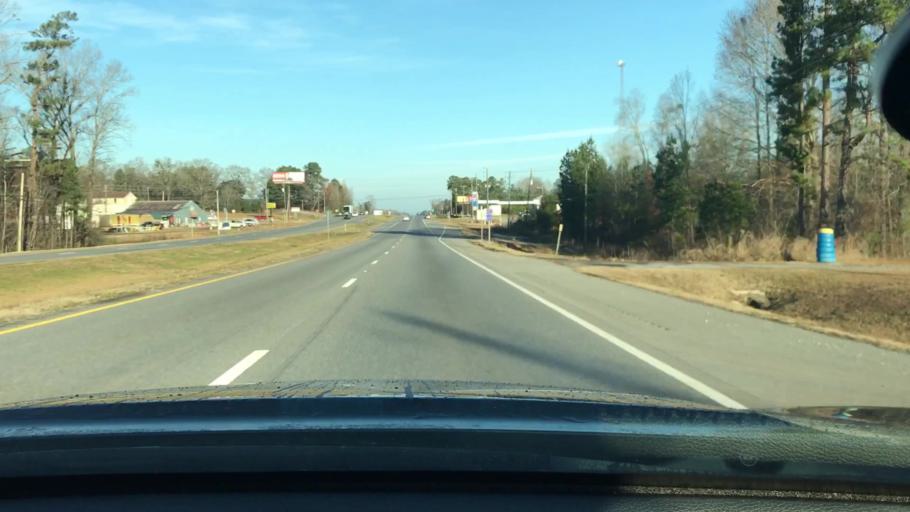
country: US
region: Alabama
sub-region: Talladega County
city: Mignon
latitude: 33.2200
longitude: -86.3187
